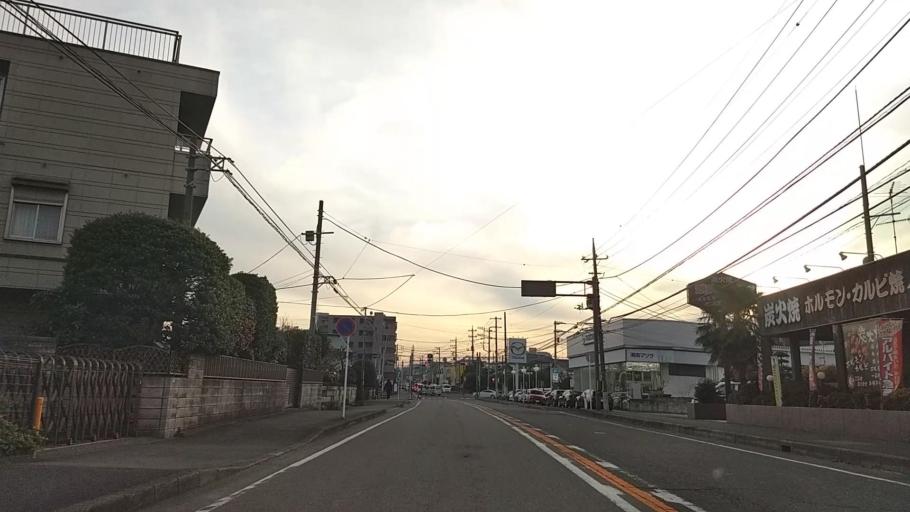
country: JP
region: Kanagawa
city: Atsugi
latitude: 35.4416
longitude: 139.3548
